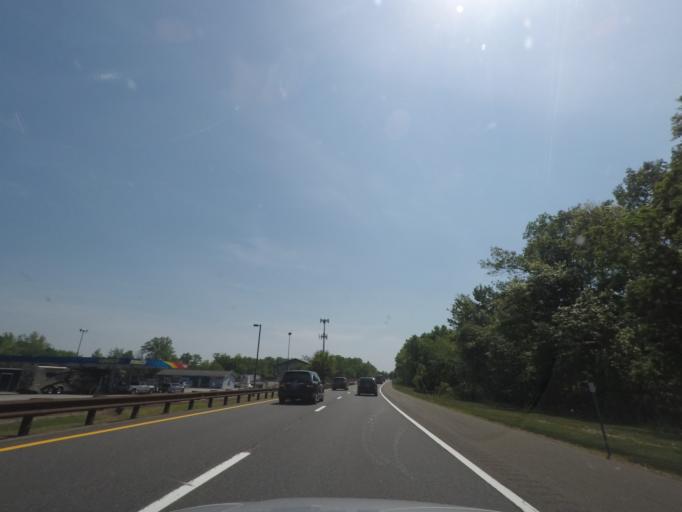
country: US
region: New Jersey
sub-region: Bergen County
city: Woodcliff Lake
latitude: 41.0471
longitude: -74.0675
